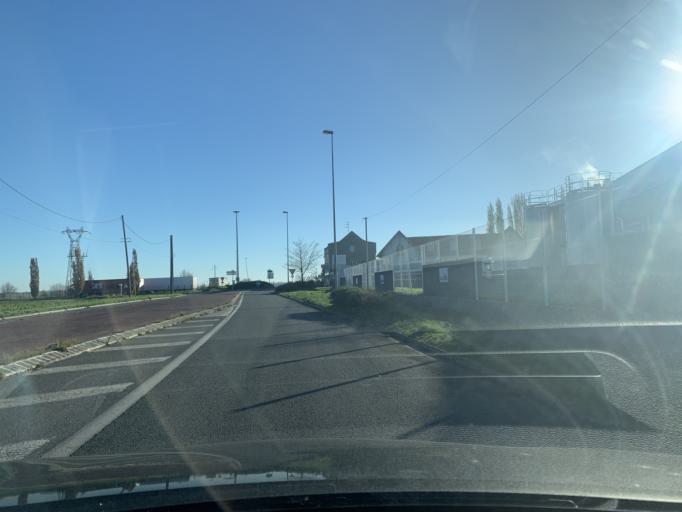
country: FR
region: Nord-Pas-de-Calais
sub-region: Departement du Nord
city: Escaudoeuvres
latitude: 50.1629
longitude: 3.2859
